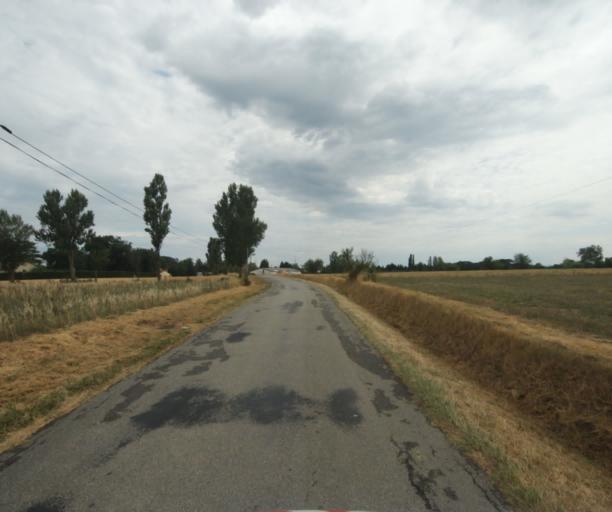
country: FR
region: Midi-Pyrenees
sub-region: Departement de la Haute-Garonne
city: Revel
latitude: 43.4488
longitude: 1.9794
